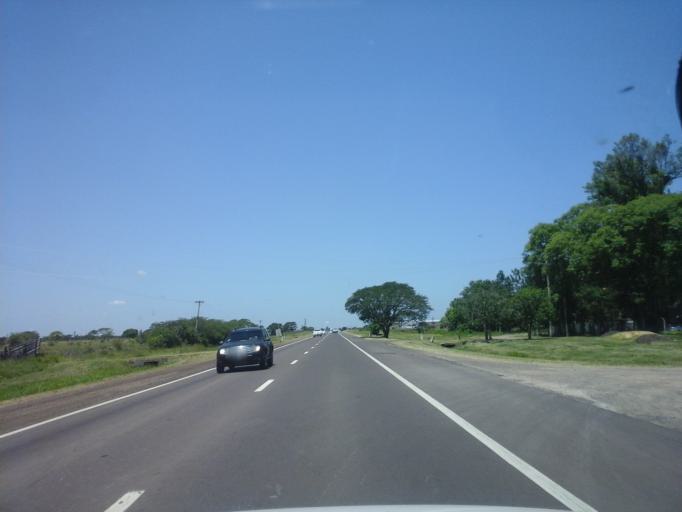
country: AR
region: Corrientes
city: Corrientes
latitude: -27.4255
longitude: -58.7128
